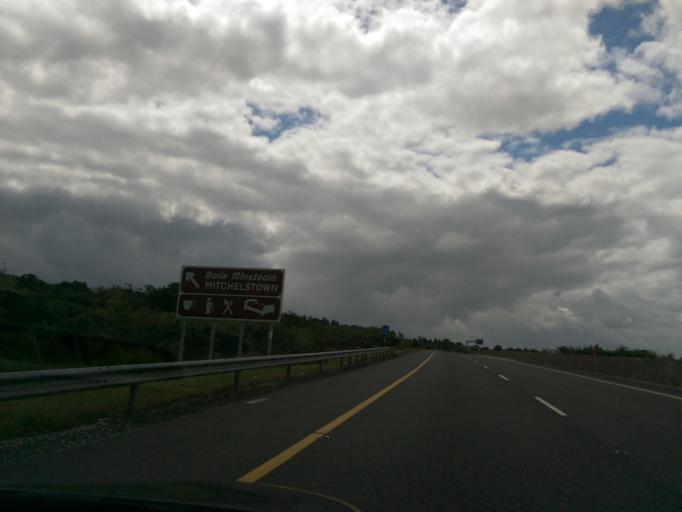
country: IE
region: Munster
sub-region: County Cork
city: Mitchelstown
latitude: 52.2444
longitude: -8.2699
